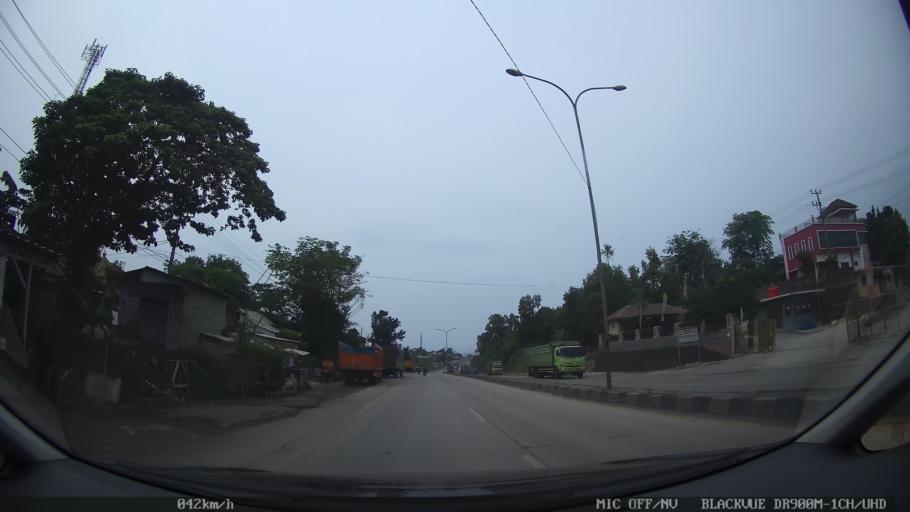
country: ID
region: Lampung
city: Bandarlampung
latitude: -5.4233
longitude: 105.2961
